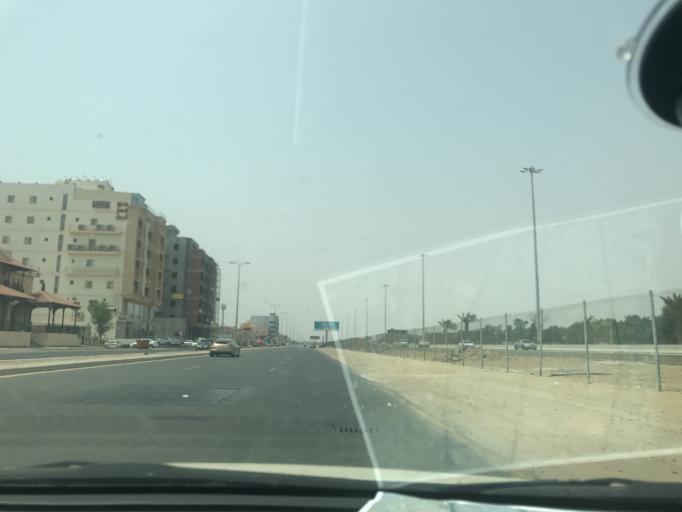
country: SA
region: Makkah
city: Jeddah
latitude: 21.6950
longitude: 39.1189
